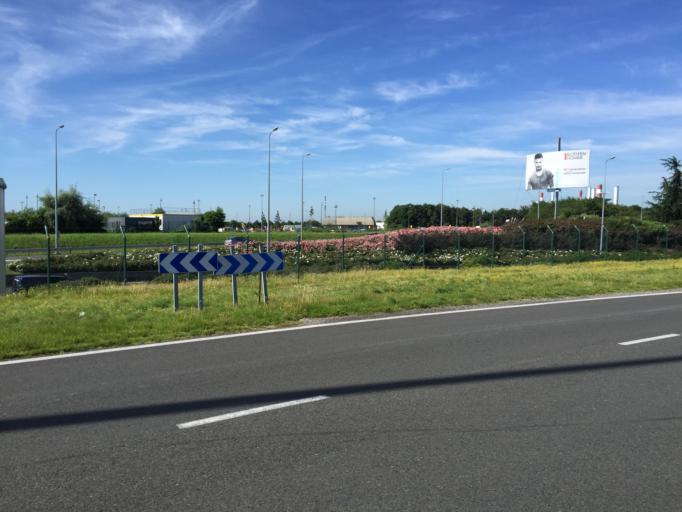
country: FR
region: Ile-de-France
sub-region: Departement du Val-d'Oise
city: Roissy-en-France
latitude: 49.0107
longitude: 2.5442
